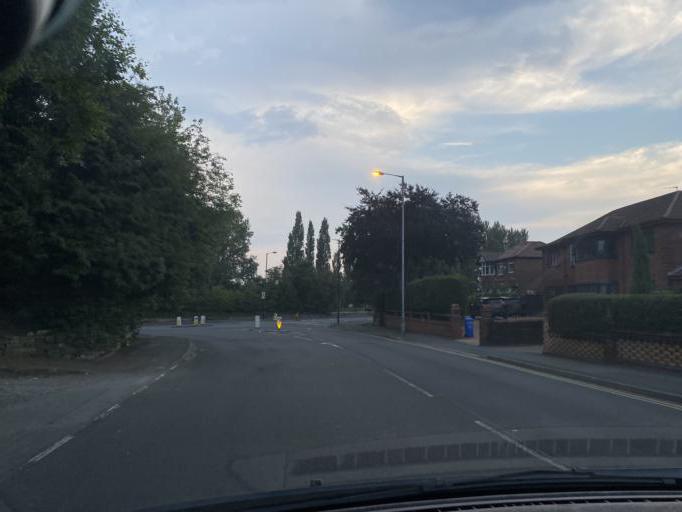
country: GB
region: England
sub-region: Borough of Tameside
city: Denton
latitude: 53.4716
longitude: -2.1239
